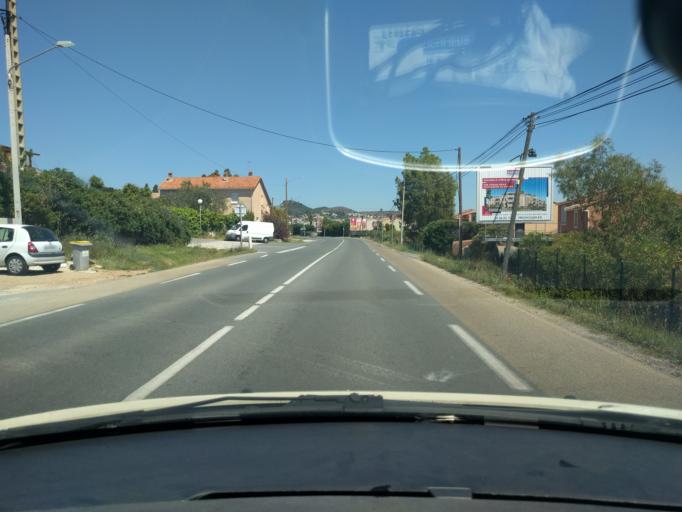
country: FR
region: Provence-Alpes-Cote d'Azur
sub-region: Departement du Var
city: Hyeres
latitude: 43.0980
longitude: 6.1316
